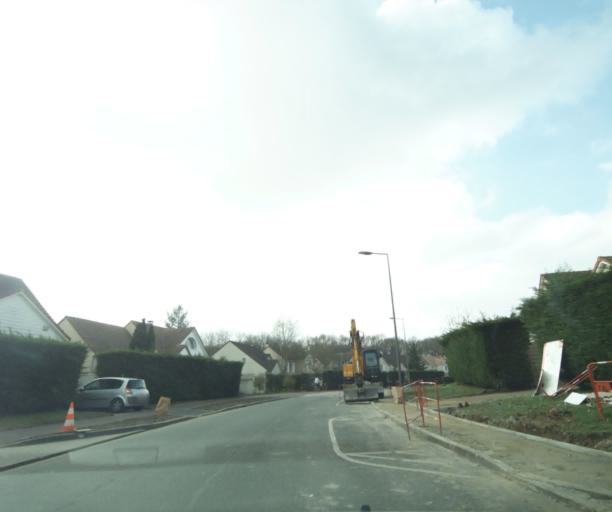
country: FR
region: Ile-de-France
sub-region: Departement du Val-d'Oise
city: Vaureal
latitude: 49.0397
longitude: 2.0225
